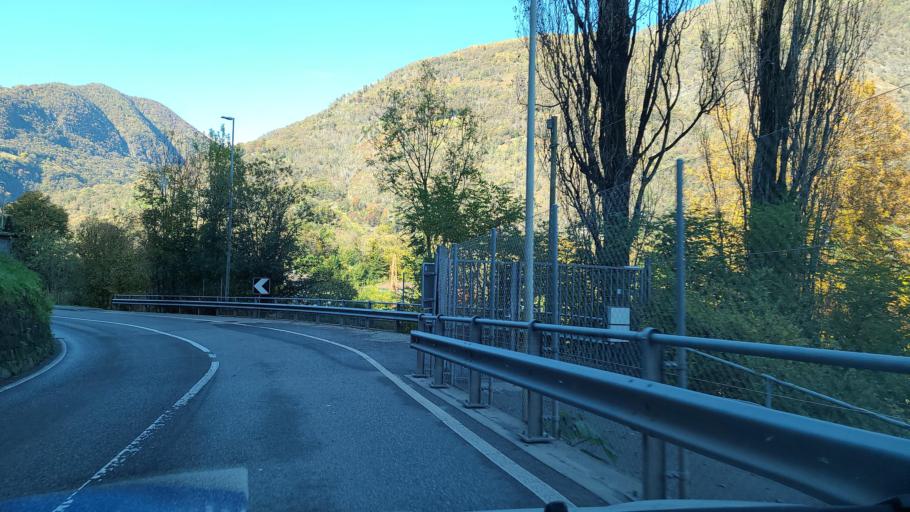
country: CH
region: Ticino
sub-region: Locarno District
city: Verscio
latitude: 46.1772
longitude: 8.7197
